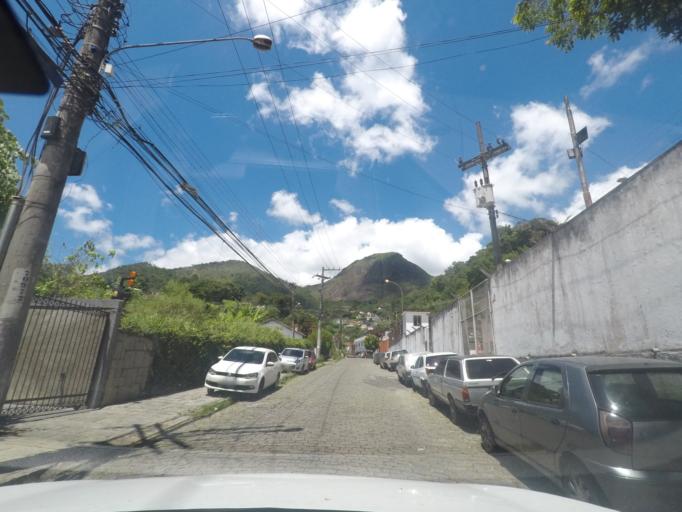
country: BR
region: Rio de Janeiro
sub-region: Teresopolis
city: Teresopolis
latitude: -22.4215
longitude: -42.9819
